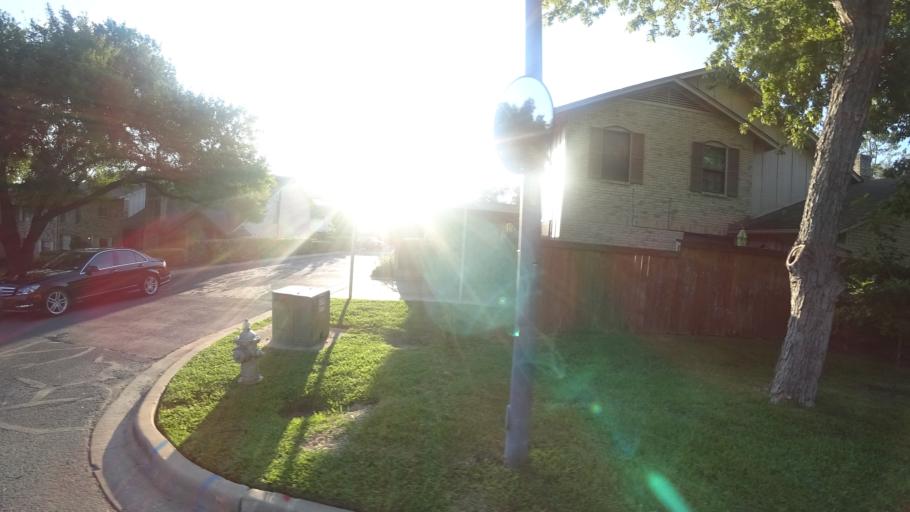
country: US
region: Texas
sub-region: Travis County
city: Austin
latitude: 30.3250
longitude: -97.6823
